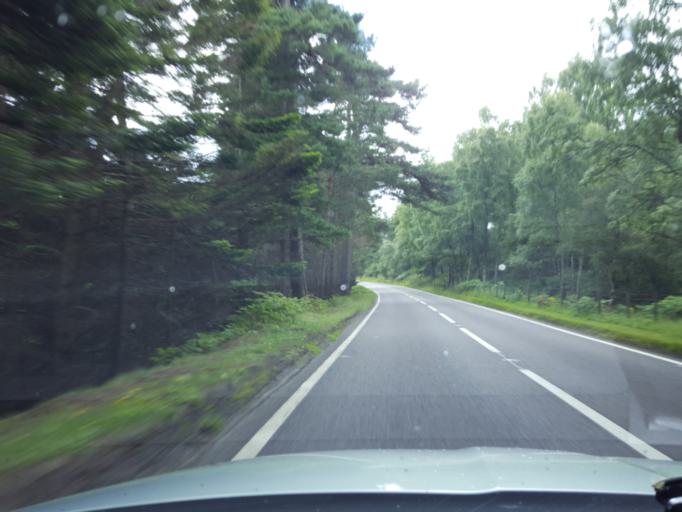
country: GB
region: Scotland
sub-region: Highland
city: Aviemore
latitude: 57.2393
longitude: -3.8057
